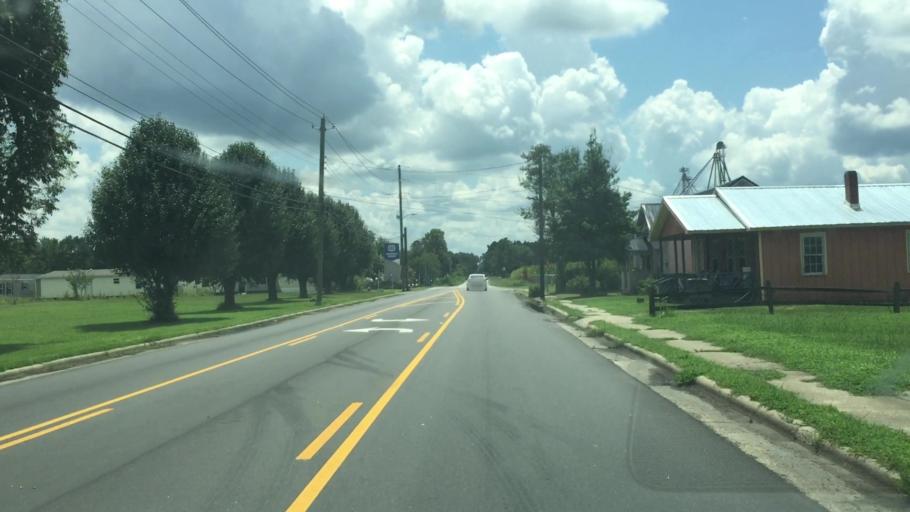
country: US
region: North Carolina
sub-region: Columbus County
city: Chadbourn
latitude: 34.3175
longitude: -78.8264
